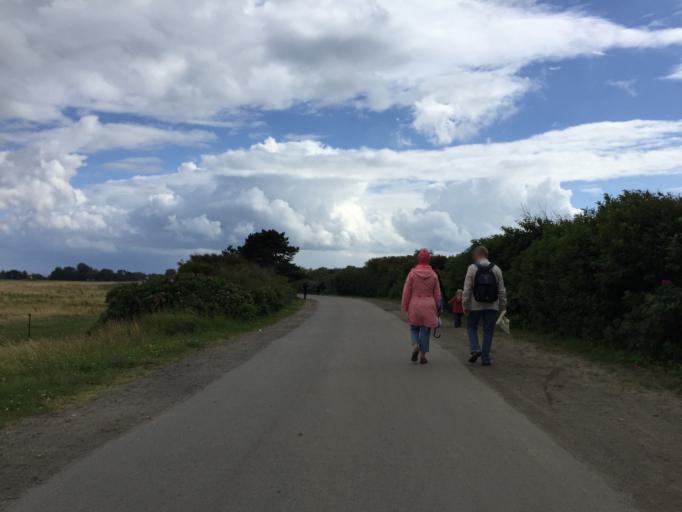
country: DE
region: Mecklenburg-Vorpommern
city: Hiddensee
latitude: 54.5804
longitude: 13.1021
